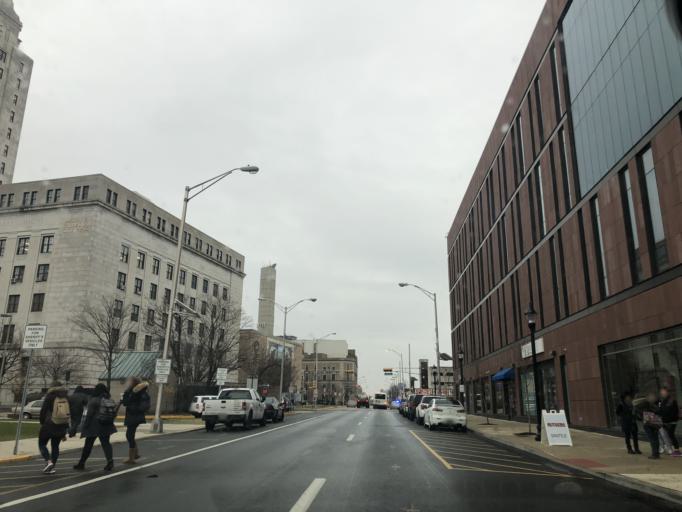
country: US
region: New Jersey
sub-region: Camden County
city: Camden
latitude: 39.9441
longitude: -75.1211
